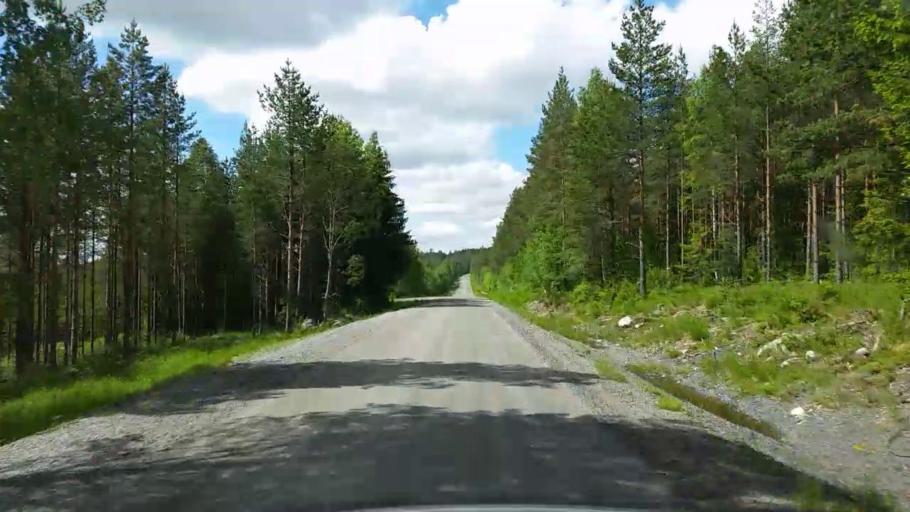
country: SE
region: Gaevleborg
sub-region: Bollnas Kommun
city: Vittsjo
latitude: 61.0887
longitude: 16.1887
